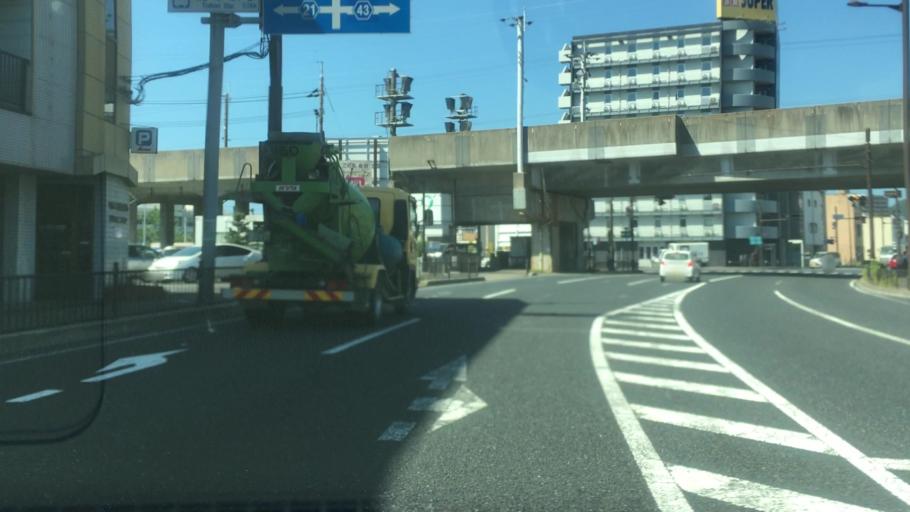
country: JP
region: Tottori
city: Tottori
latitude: 35.4947
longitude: 134.2229
